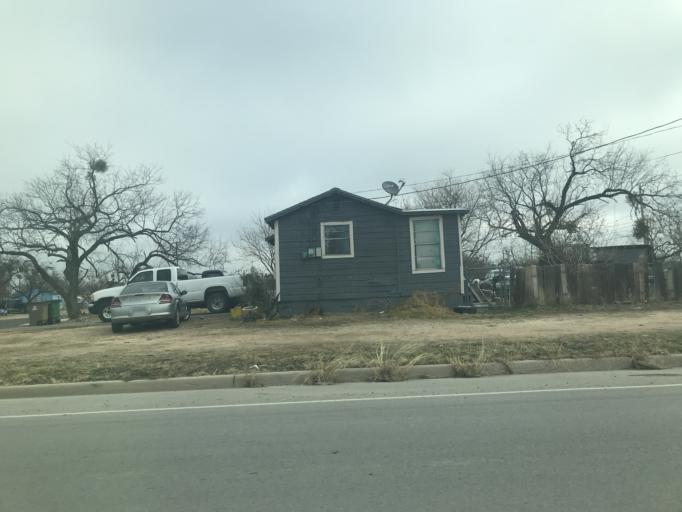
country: US
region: Texas
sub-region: Tom Green County
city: San Angelo
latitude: 31.4746
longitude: -100.4496
